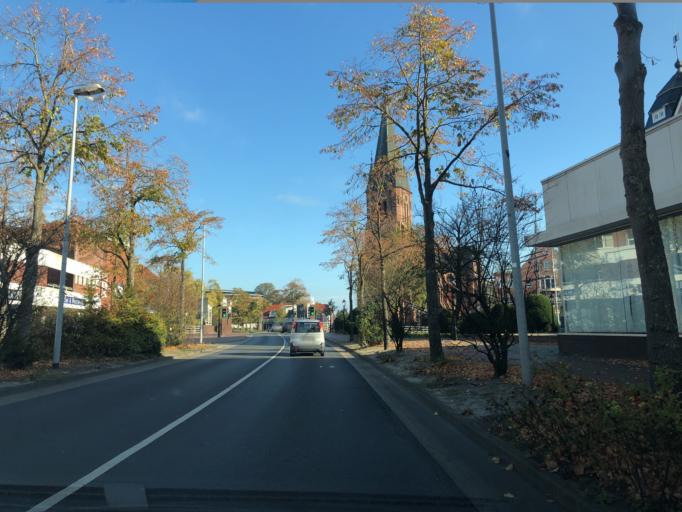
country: DE
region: Lower Saxony
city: Papenburg
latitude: 53.0780
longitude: 7.3930
